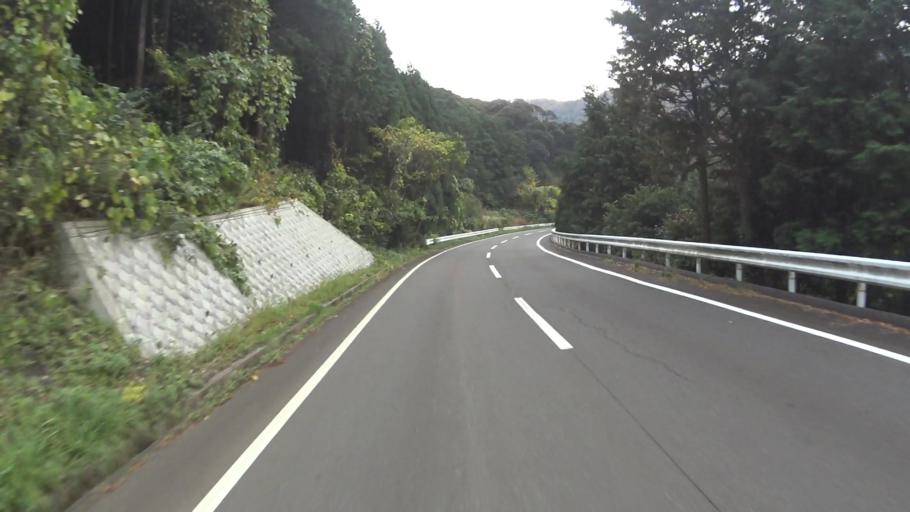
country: JP
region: Kyoto
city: Maizuru
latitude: 35.5643
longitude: 135.4571
